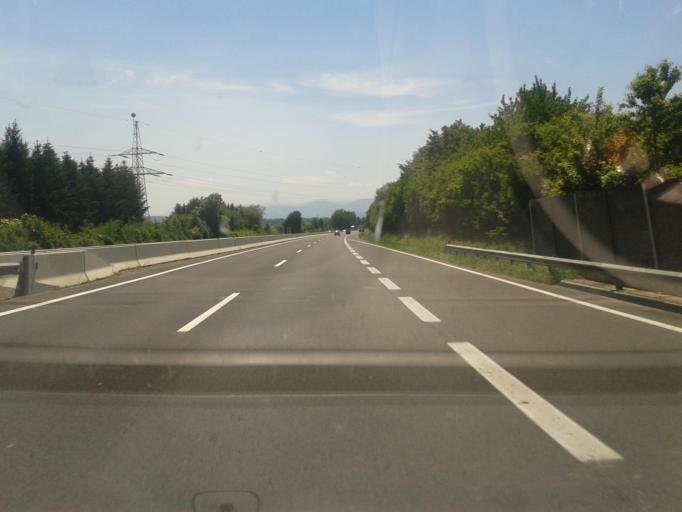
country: AT
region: Carinthia
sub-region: Politischer Bezirk Wolfsberg
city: Wolfsberg
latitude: 46.8185
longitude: 14.8219
